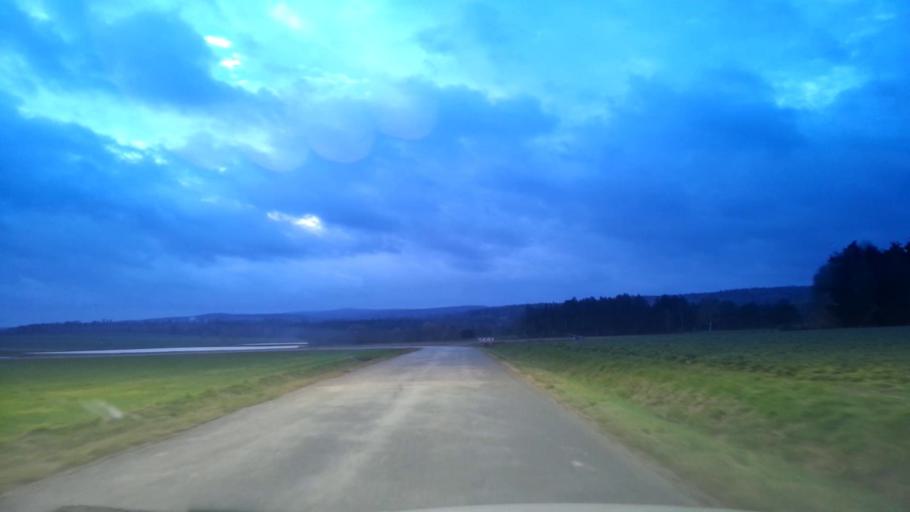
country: DE
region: Bavaria
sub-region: Upper Palatinate
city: Pechbrunn
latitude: 49.9413
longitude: 12.1829
